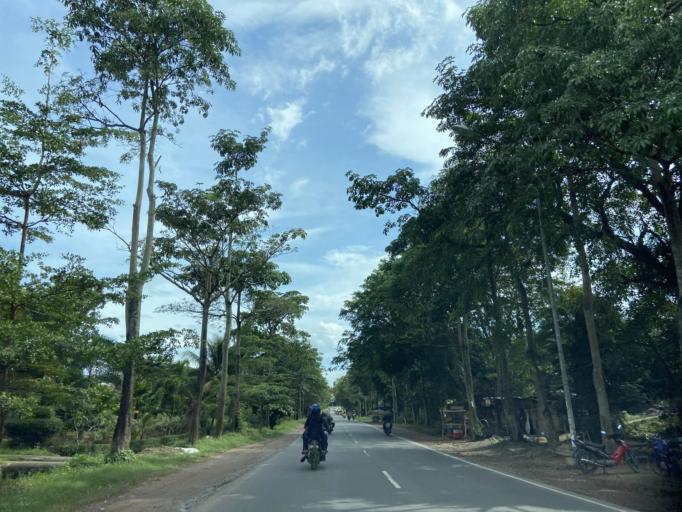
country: SG
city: Singapore
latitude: 1.0559
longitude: 103.9600
